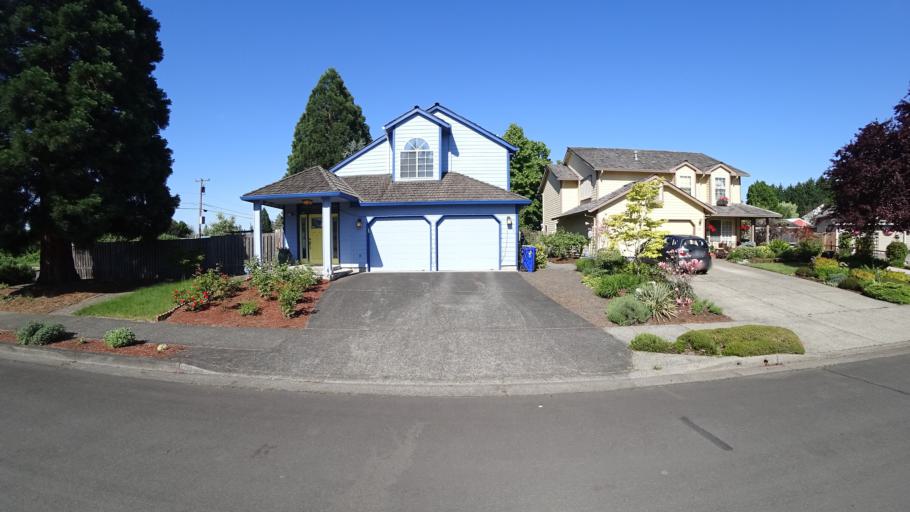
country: US
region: Oregon
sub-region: Washington County
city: Rockcreek
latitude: 45.5242
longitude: -122.9163
